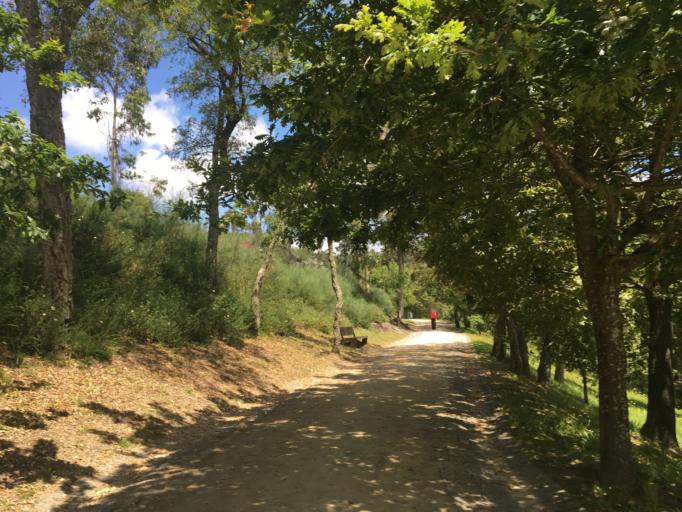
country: PT
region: Porto
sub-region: Maia
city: Anta
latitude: 41.2887
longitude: -8.6138
